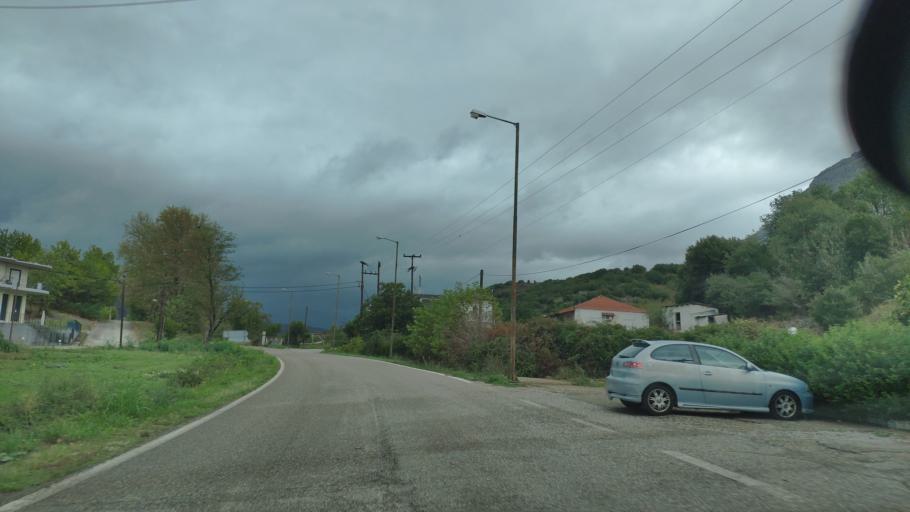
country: GR
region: West Greece
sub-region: Nomos Aitolias kai Akarnanias
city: Krikellos
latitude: 38.9739
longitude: 21.3305
